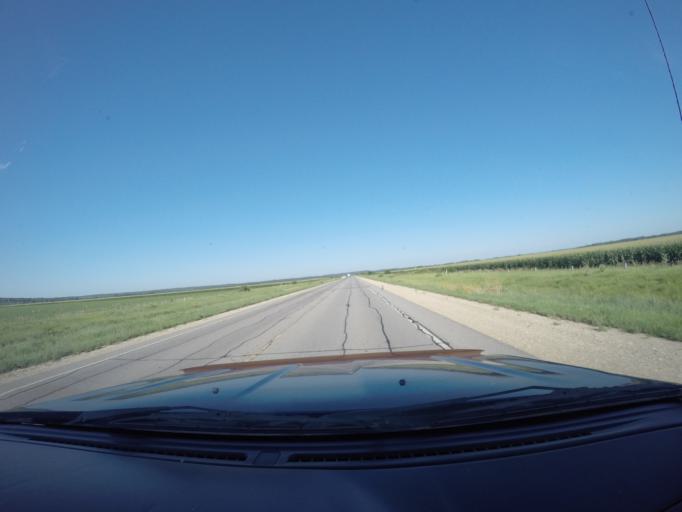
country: US
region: Kansas
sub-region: Jefferson County
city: Oskaloosa
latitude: 39.0872
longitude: -95.4498
